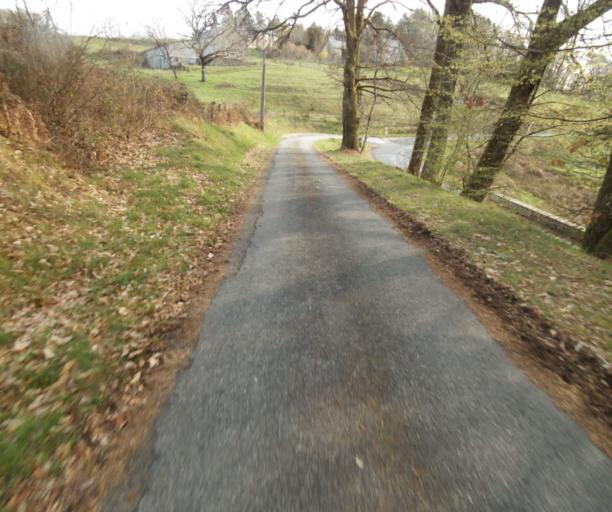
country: FR
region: Limousin
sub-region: Departement de la Correze
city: Correze
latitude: 45.3641
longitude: 1.8618
